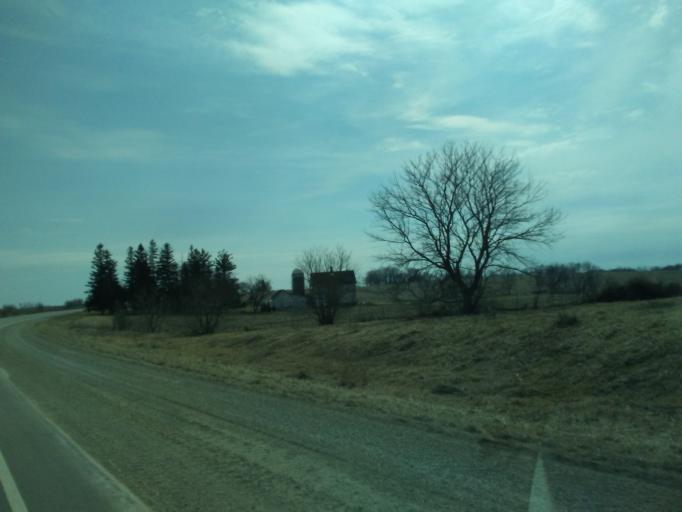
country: US
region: Iowa
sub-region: Winneshiek County
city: Decorah
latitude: 43.4492
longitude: -91.8634
